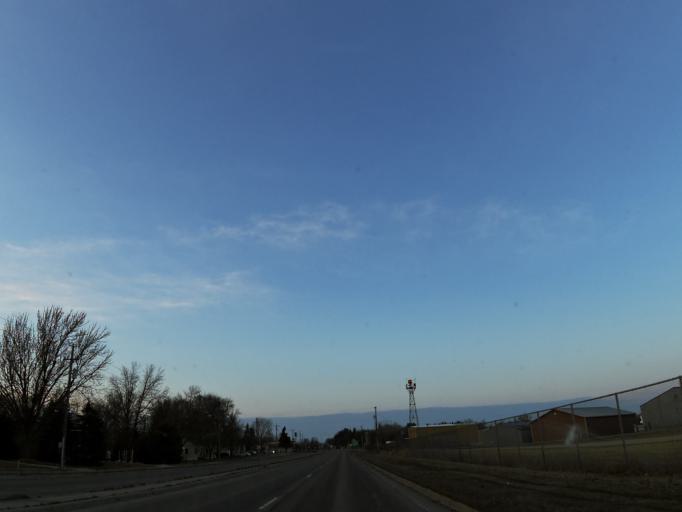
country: US
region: Minnesota
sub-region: Mower County
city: Austin
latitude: 43.6700
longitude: -92.9393
